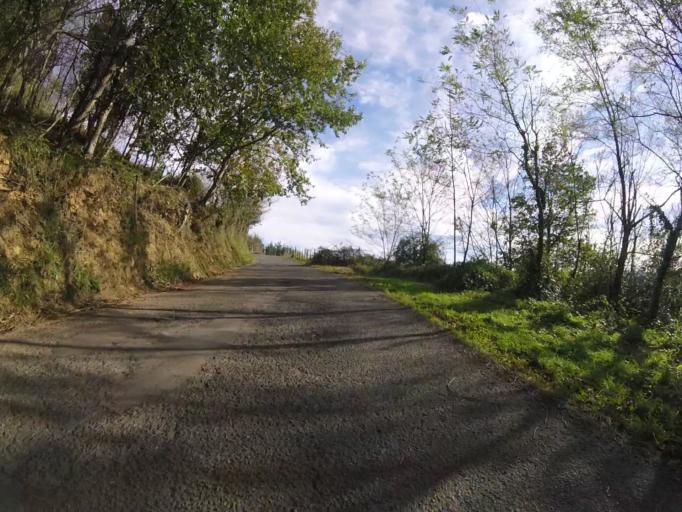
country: ES
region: Basque Country
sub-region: Provincia de Guipuzcoa
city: Orio
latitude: 43.2881
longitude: -2.0969
